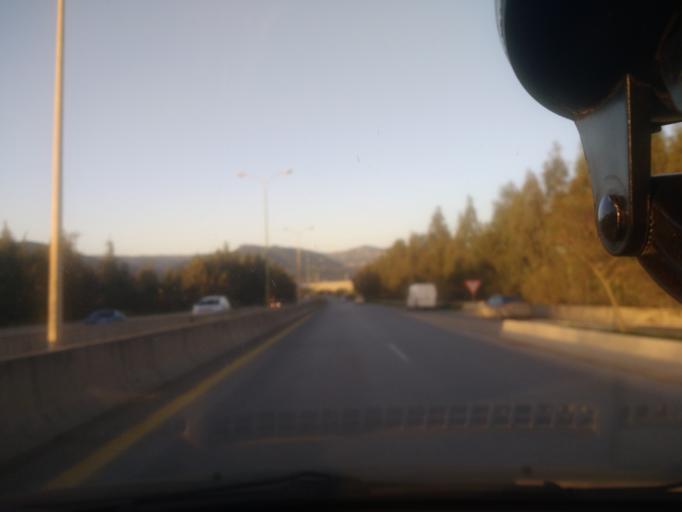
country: DZ
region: Tizi Ouzou
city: Tizi Ouzou
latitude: 36.7433
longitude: 4.0100
